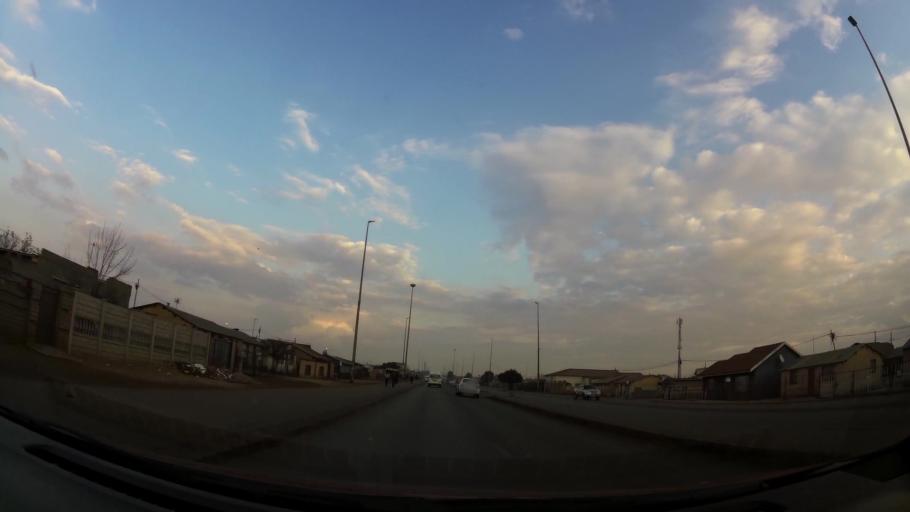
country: ZA
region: Gauteng
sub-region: City of Johannesburg Metropolitan Municipality
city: Orange Farm
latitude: -26.5645
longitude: 27.8344
